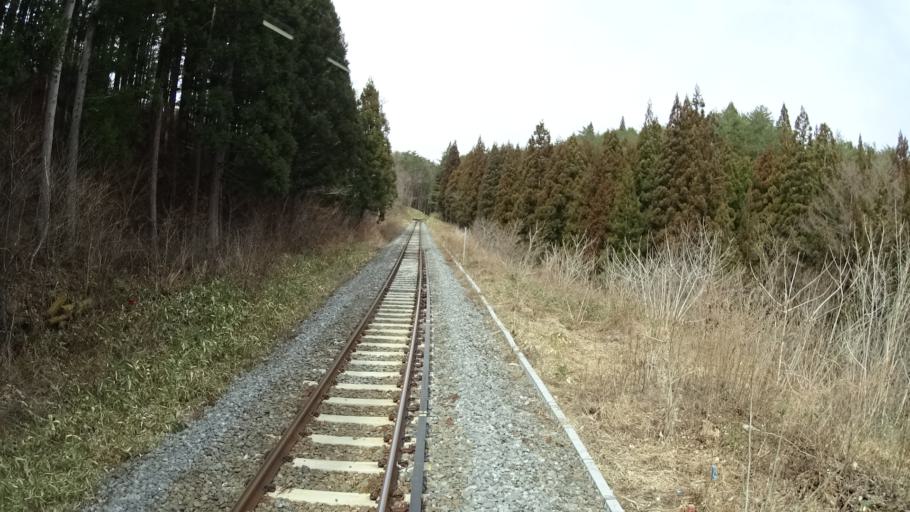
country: JP
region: Iwate
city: Yamada
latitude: 39.5010
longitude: 141.9286
